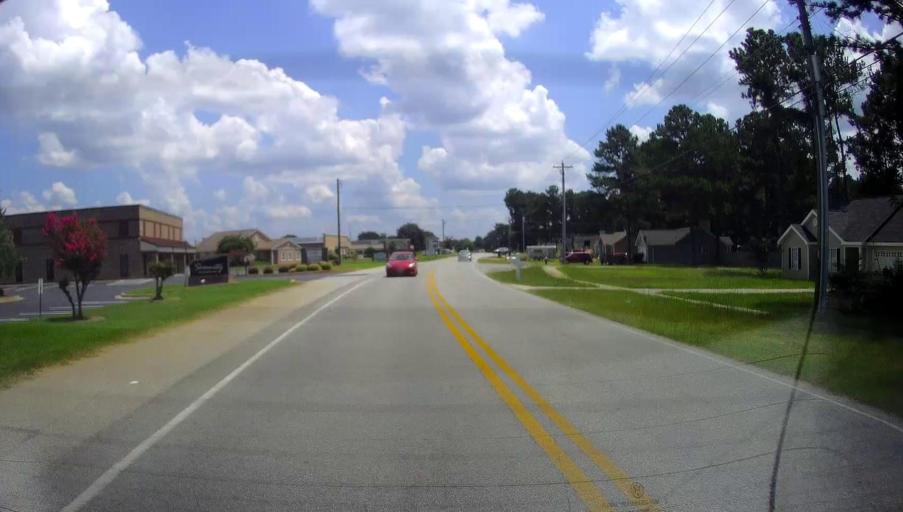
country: US
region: Georgia
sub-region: Houston County
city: Centerville
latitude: 32.6096
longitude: -83.6856
